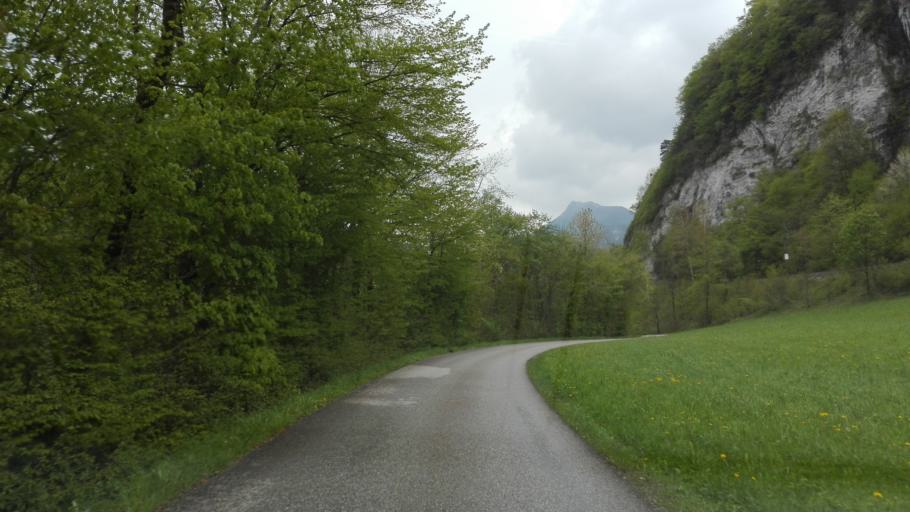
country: AT
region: Upper Austria
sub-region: Politischer Bezirk Steyr-Land
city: Losenstein
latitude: 47.9285
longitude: 14.4110
